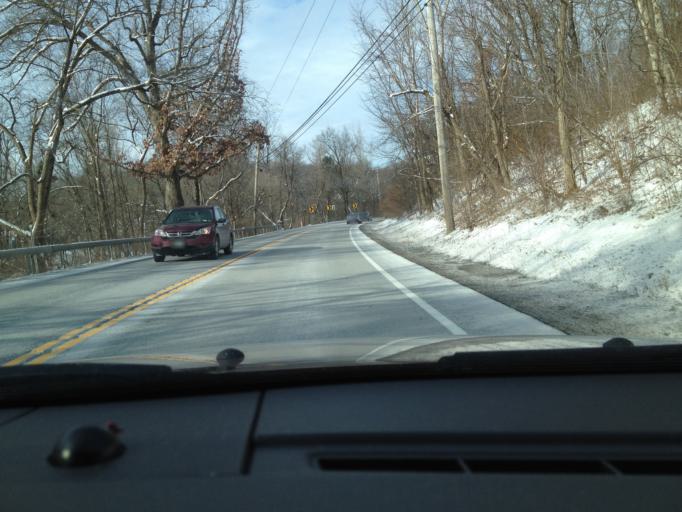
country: US
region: New York
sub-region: Rensselaer County
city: West Sand Lake
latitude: 42.6472
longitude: -73.6428
